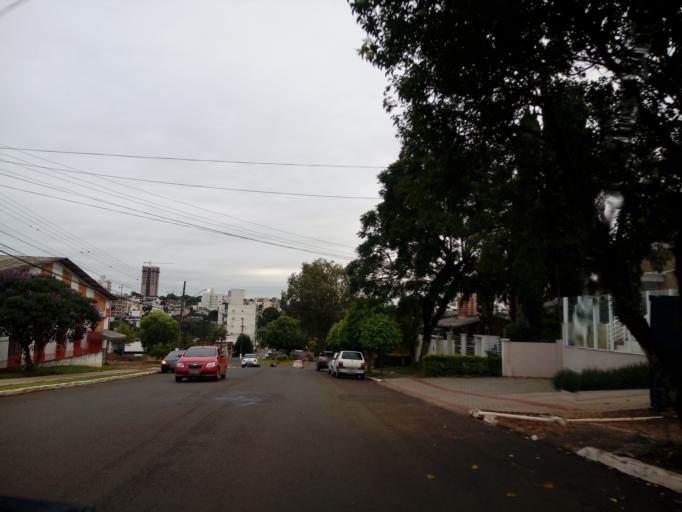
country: BR
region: Santa Catarina
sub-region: Chapeco
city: Chapeco
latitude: -27.0994
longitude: -52.6061
